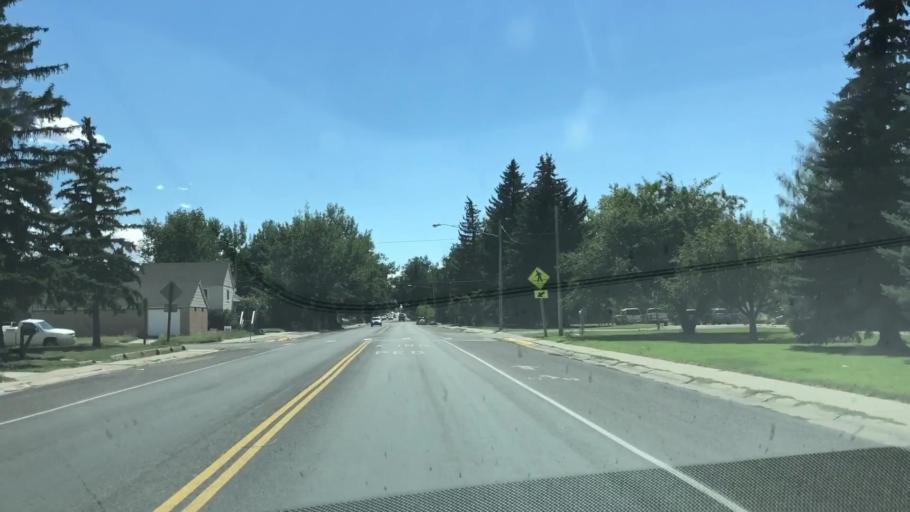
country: US
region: Wyoming
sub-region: Albany County
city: Laramie
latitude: 41.3214
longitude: -105.5846
